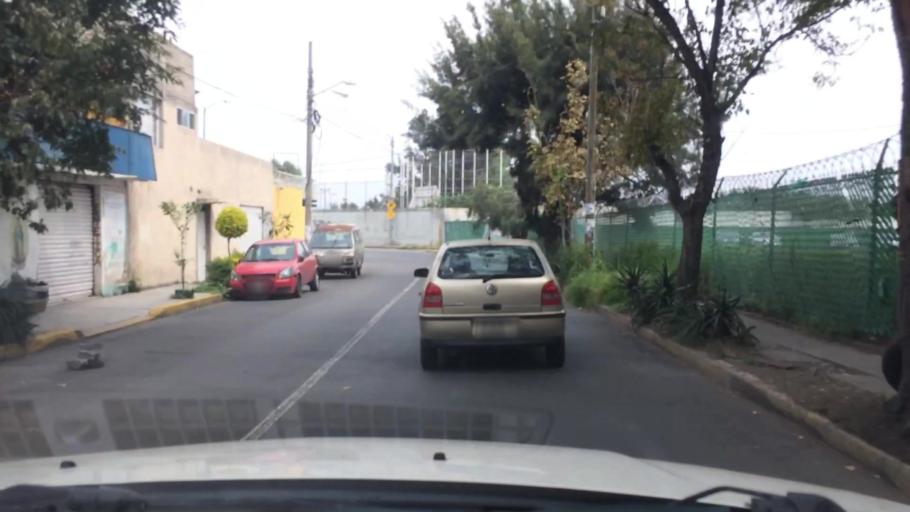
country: MX
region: Mexico City
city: Xochimilco
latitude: 19.2712
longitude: -99.1244
